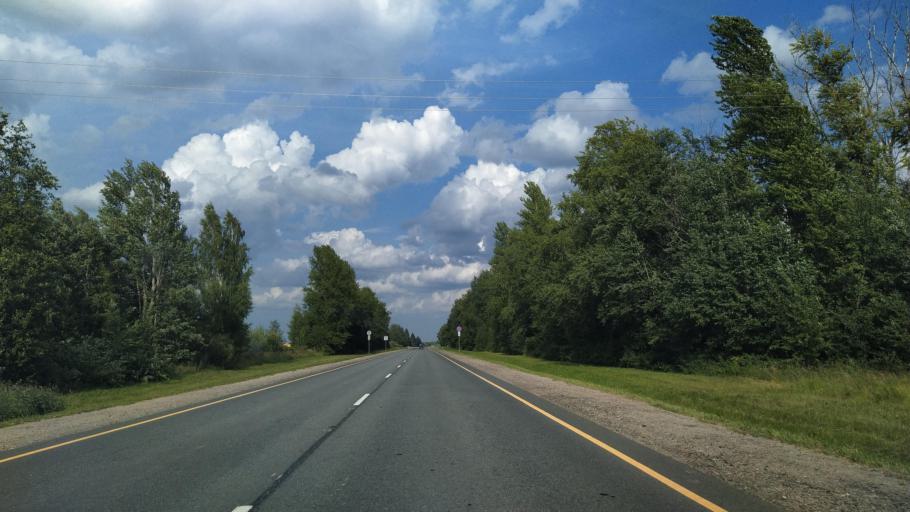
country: RU
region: Novgorod
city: Shimsk
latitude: 58.1878
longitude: 30.5570
